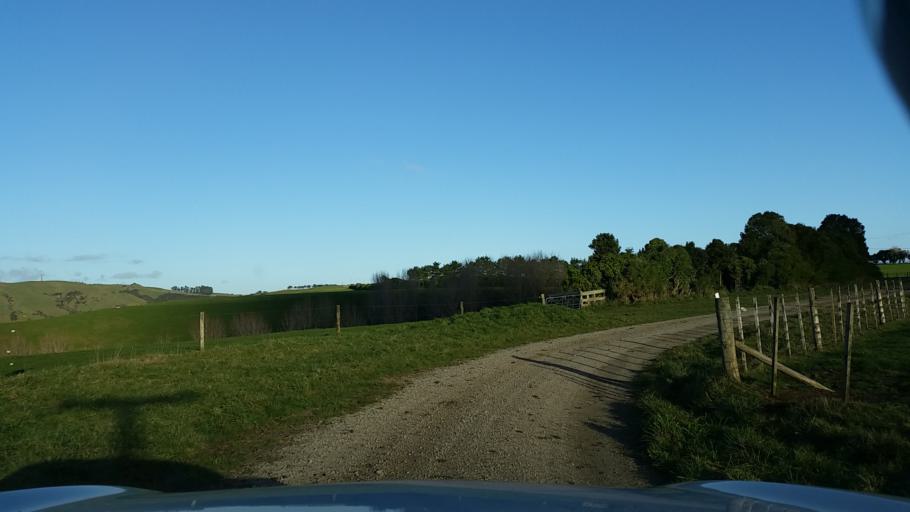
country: NZ
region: Taranaki
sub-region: South Taranaki District
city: Patea
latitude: -39.6177
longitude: 174.4980
